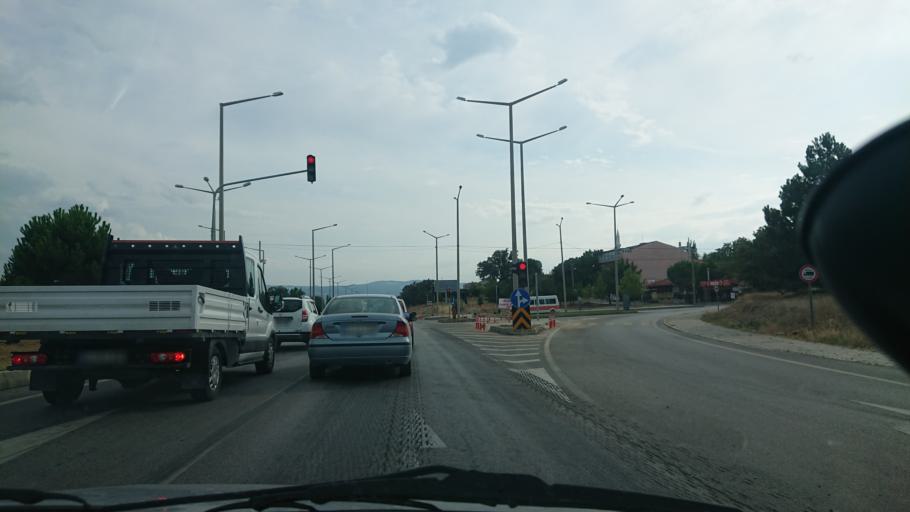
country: TR
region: Kuetahya
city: Gediz
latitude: 39.0004
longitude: 29.4036
